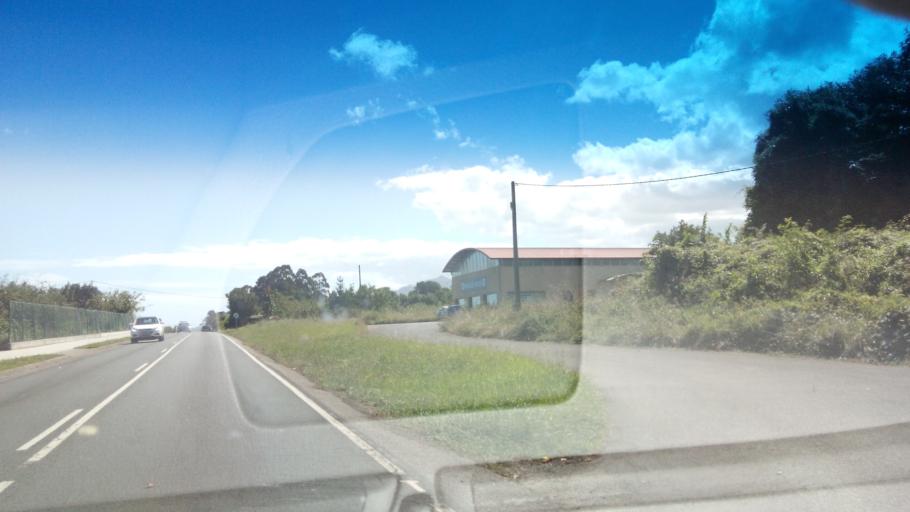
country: ES
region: Asturias
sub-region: Province of Asturias
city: Colunga
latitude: 43.4831
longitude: -5.2502
